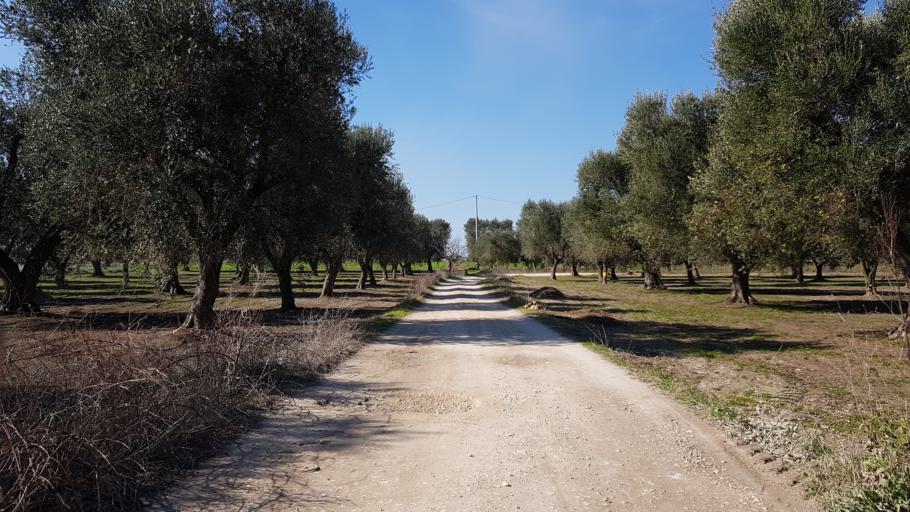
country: IT
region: Apulia
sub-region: Provincia di Brindisi
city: Mesagne
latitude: 40.6180
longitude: 17.8022
